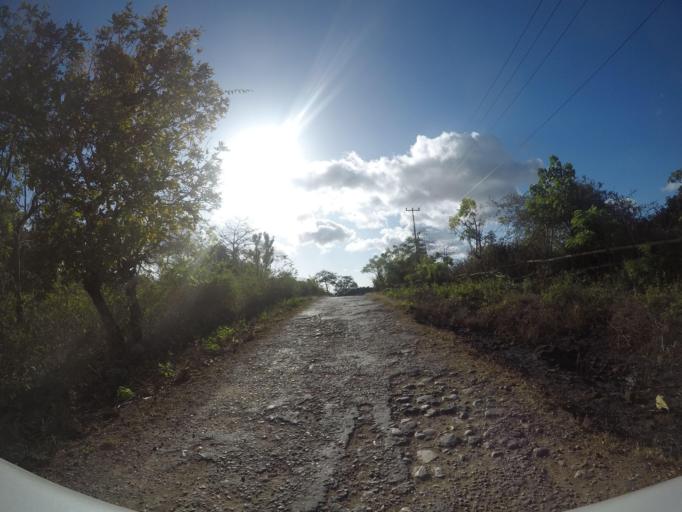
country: TL
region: Lautem
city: Lospalos
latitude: -8.4396
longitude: 126.8603
